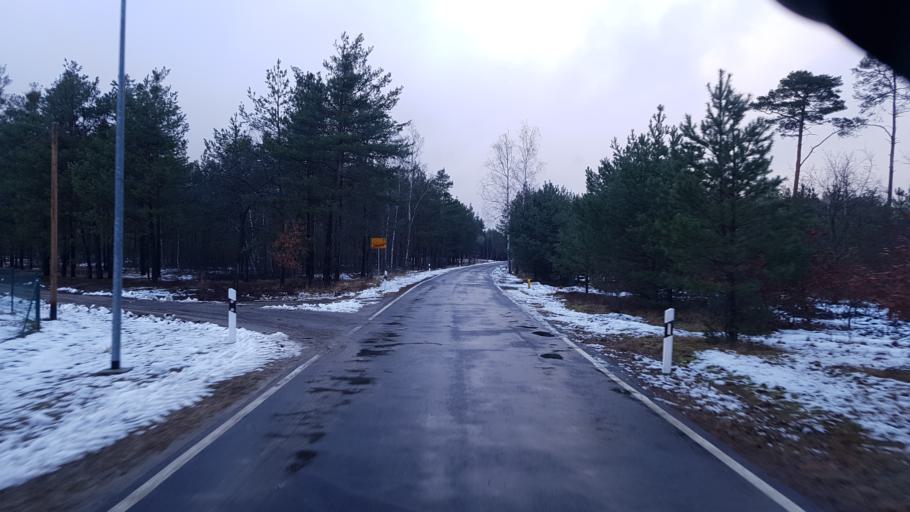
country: DE
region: Brandenburg
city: Janschwalde
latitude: 51.8423
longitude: 14.5085
